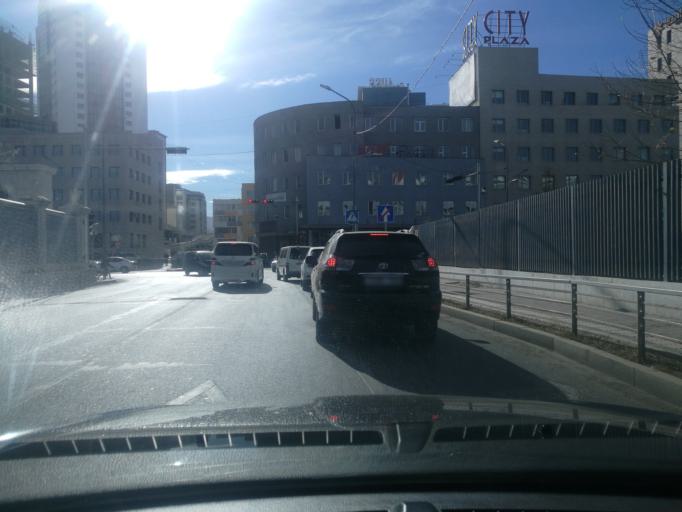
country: MN
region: Ulaanbaatar
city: Ulaanbaatar
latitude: 47.9156
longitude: 106.9130
